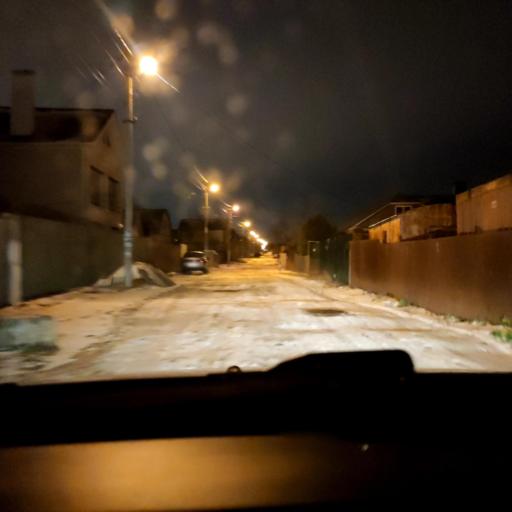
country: RU
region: Voronezj
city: Pridonskoy
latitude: 51.6844
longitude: 39.0705
